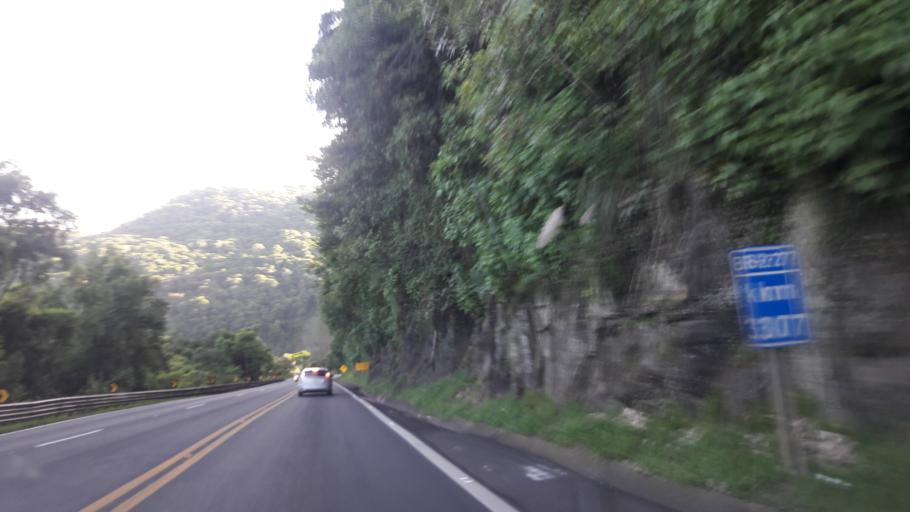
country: BR
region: Parana
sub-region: Prudentopolis
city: Prudentopolis
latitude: -25.3179
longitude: -51.1949
